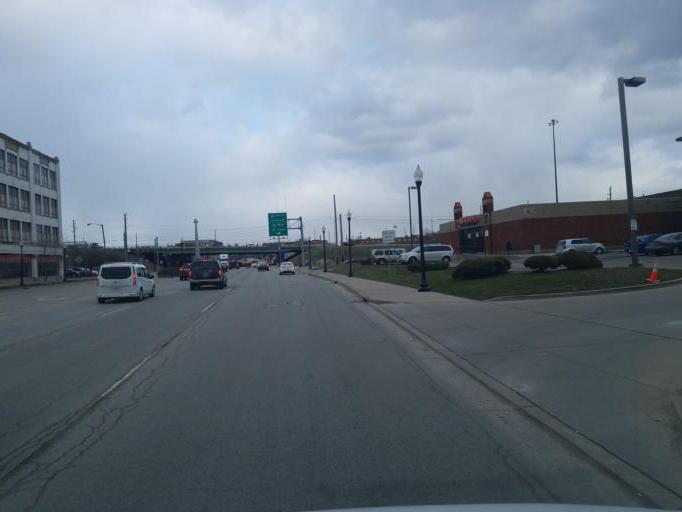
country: US
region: Indiana
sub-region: Marion County
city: Indianapolis
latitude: 39.7668
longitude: -86.1452
